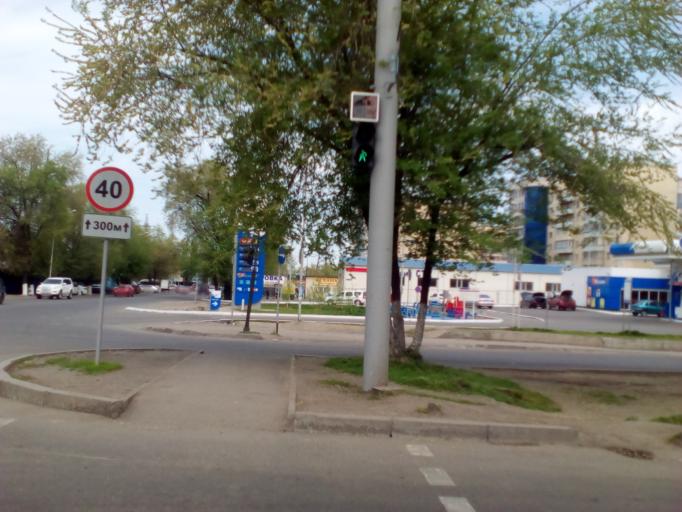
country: KZ
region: Almaty Qalasy
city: Almaty
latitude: 43.2379
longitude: 76.8240
